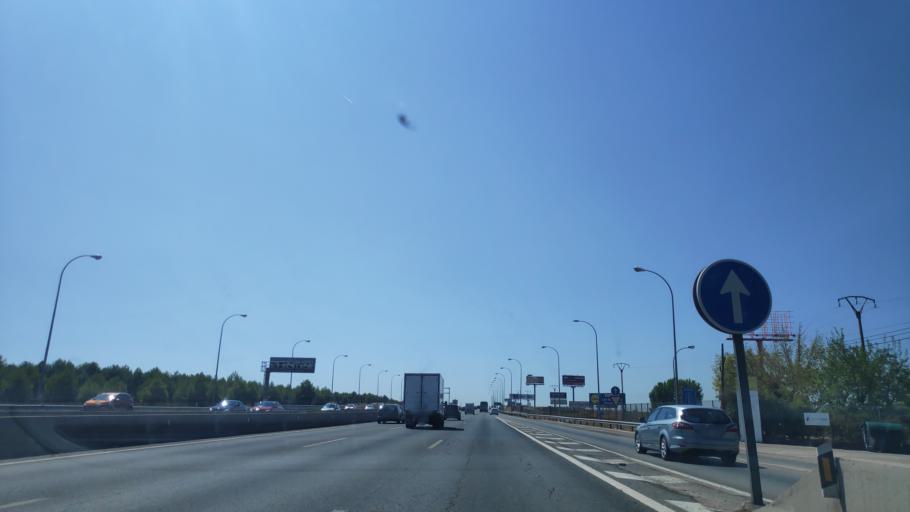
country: ES
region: Madrid
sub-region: Provincia de Madrid
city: Villaverde
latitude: 40.3601
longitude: -3.7215
